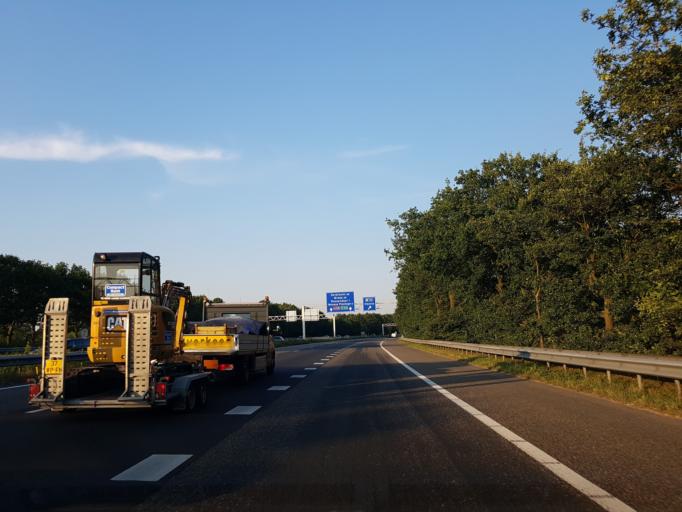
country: NL
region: North Brabant
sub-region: Gemeente Bergen op Zoom
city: Bergen op Zoom
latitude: 51.5060
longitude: 4.3543
